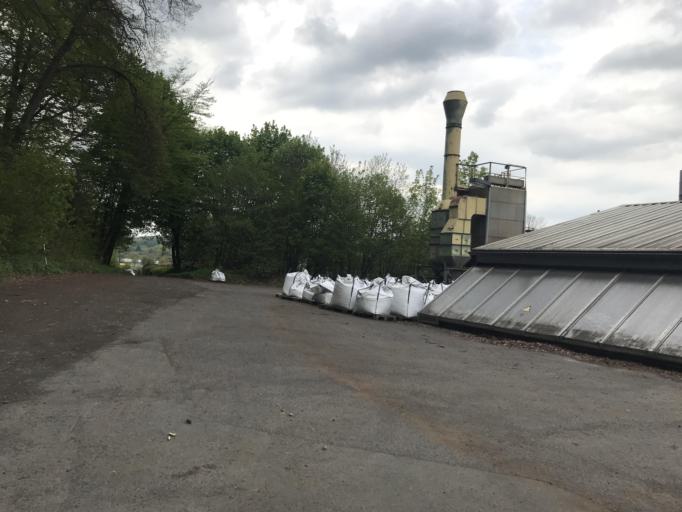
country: DE
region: Hesse
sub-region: Regierungsbezirk Giessen
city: Laubach
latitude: 50.5192
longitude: 8.9837
